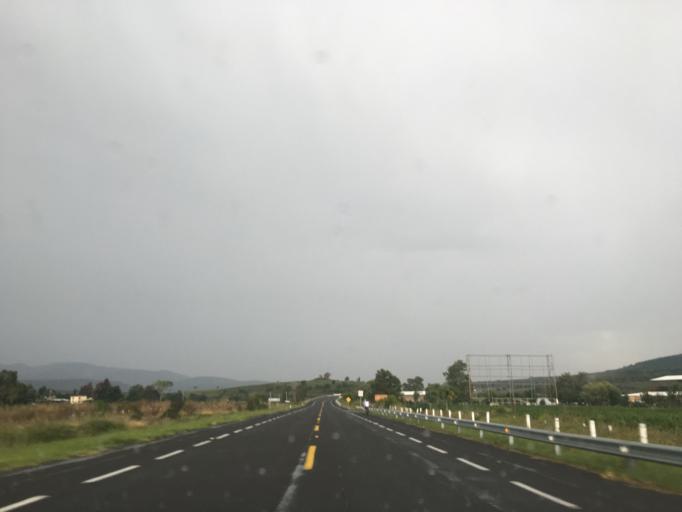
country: MX
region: Michoacan
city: Alvaro Obregon
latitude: 19.8231
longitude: -101.0115
